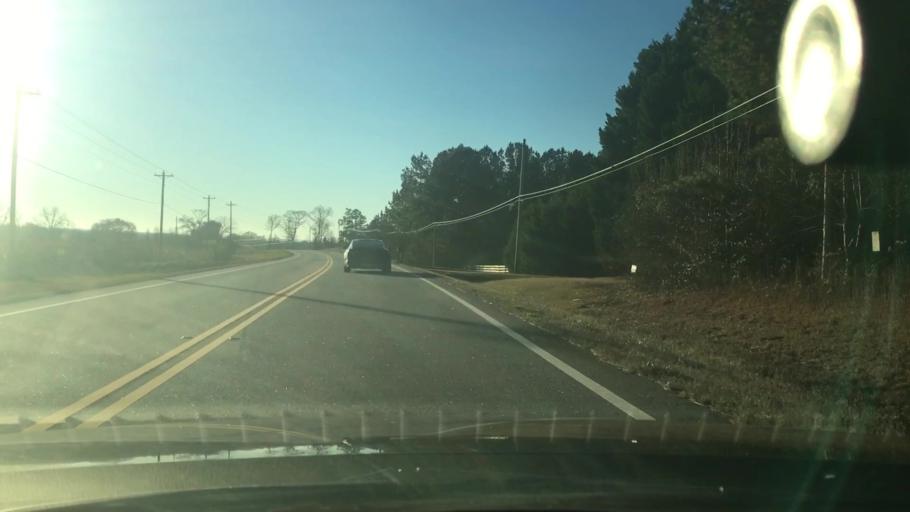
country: US
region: Georgia
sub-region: Coweta County
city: Senoia
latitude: 33.2781
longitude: -84.5343
